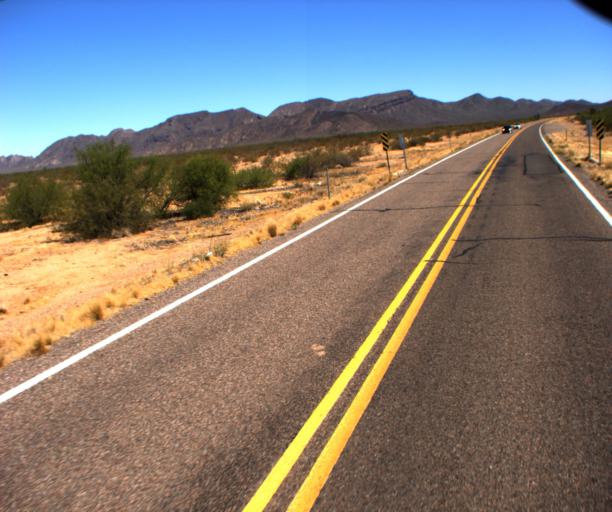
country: US
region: Arizona
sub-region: Yavapai County
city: Congress
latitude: 33.9834
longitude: -113.1384
